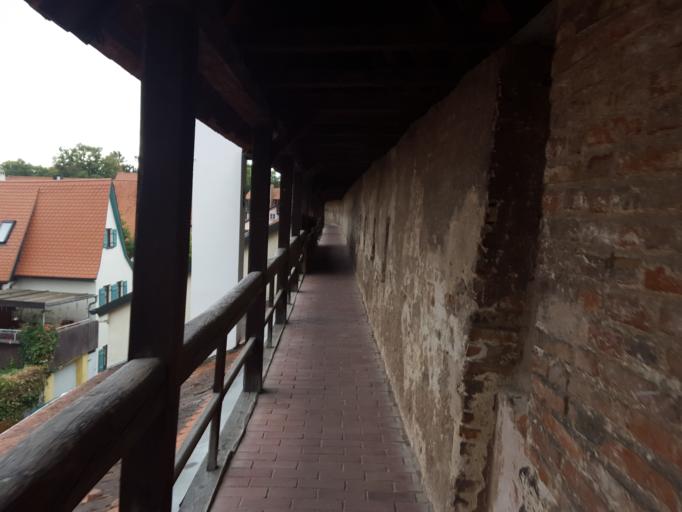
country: DE
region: Bavaria
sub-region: Swabia
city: Noerdlingen
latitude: 48.8480
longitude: 10.4849
